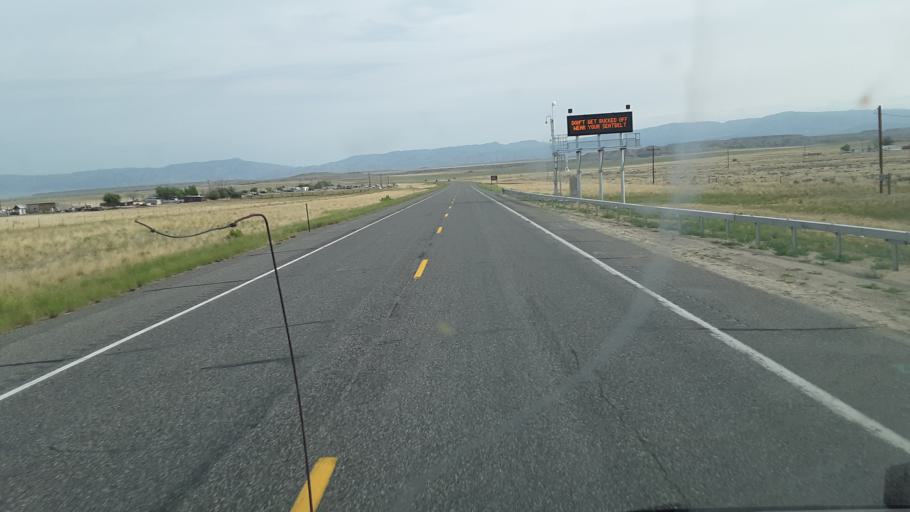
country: US
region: Wyoming
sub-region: Fremont County
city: Riverton
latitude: 43.2524
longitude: -108.1103
